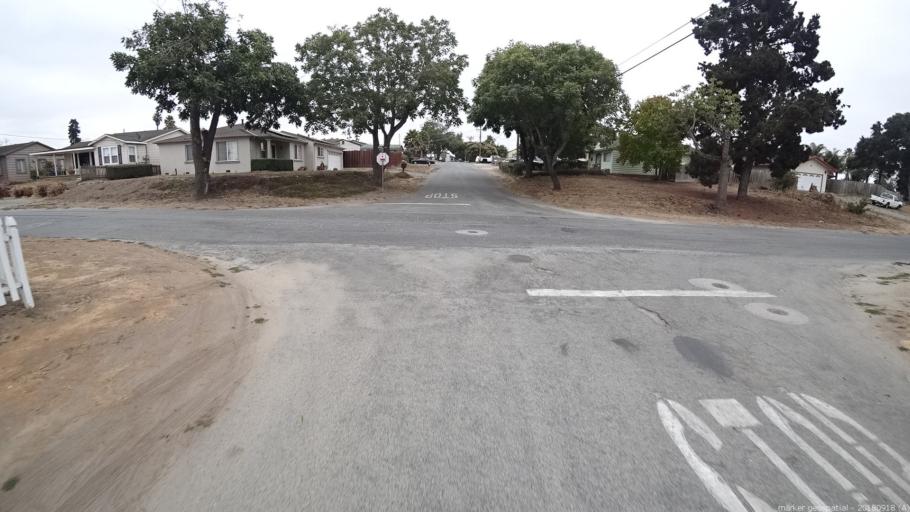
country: US
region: California
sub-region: Monterey County
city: Boronda
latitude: 36.7320
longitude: -121.6417
